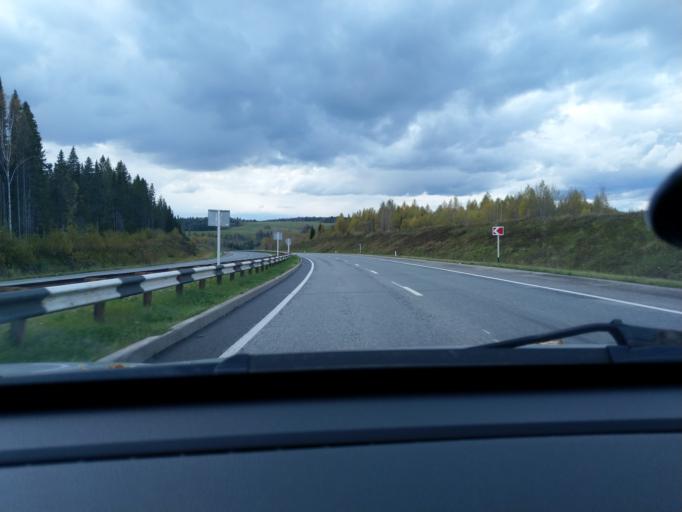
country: RU
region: Perm
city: Polazna
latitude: 58.3104
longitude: 56.4804
